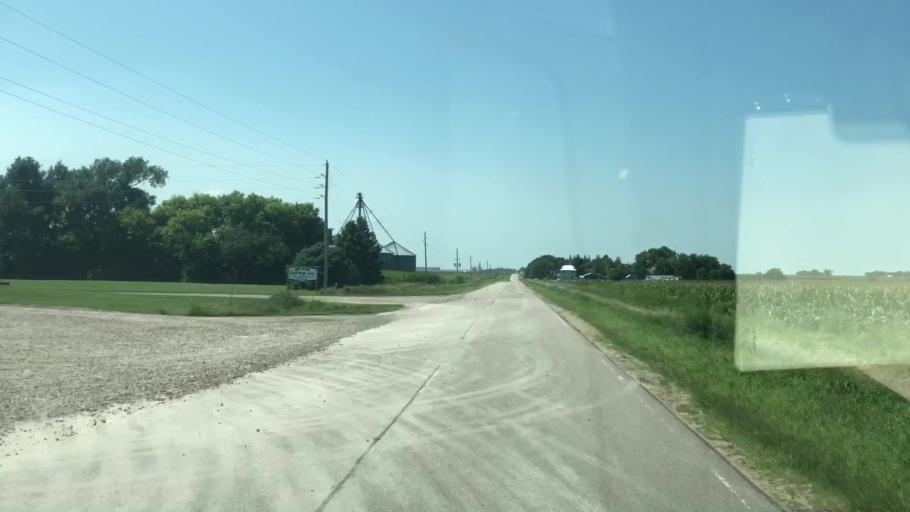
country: US
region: Iowa
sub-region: O'Brien County
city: Sheldon
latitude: 43.2443
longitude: -95.7754
